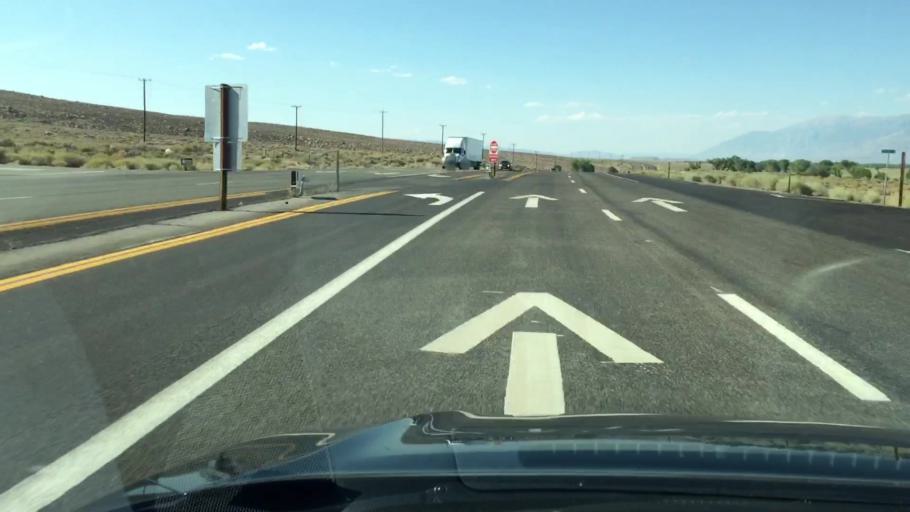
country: US
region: California
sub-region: Inyo County
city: Bishop
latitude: 37.2816
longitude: -118.3728
